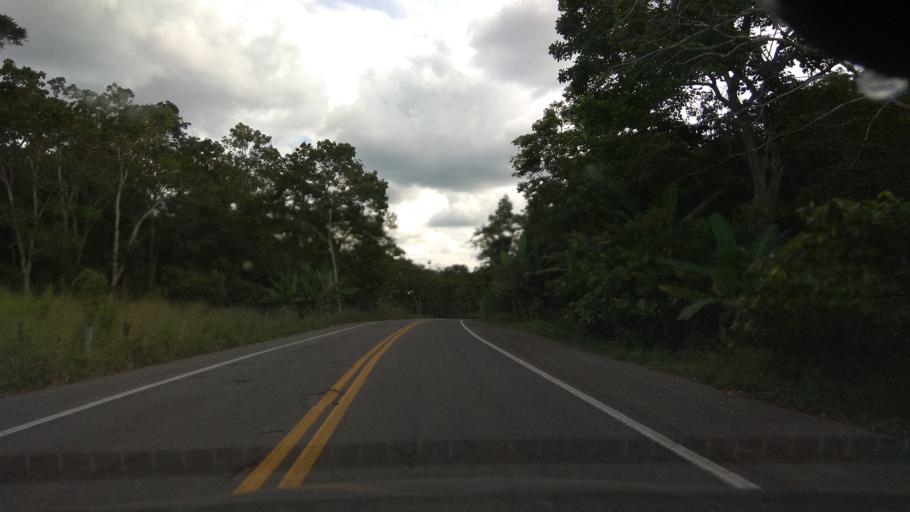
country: BR
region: Bahia
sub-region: Ubaitaba
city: Ubaitaba
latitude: -14.2623
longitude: -39.3368
